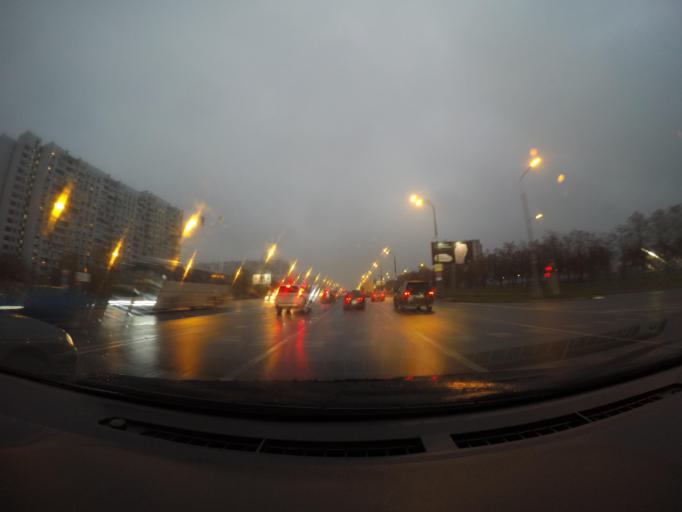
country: RU
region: Moscow
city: Nagornyy
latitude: 55.6221
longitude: 37.6149
